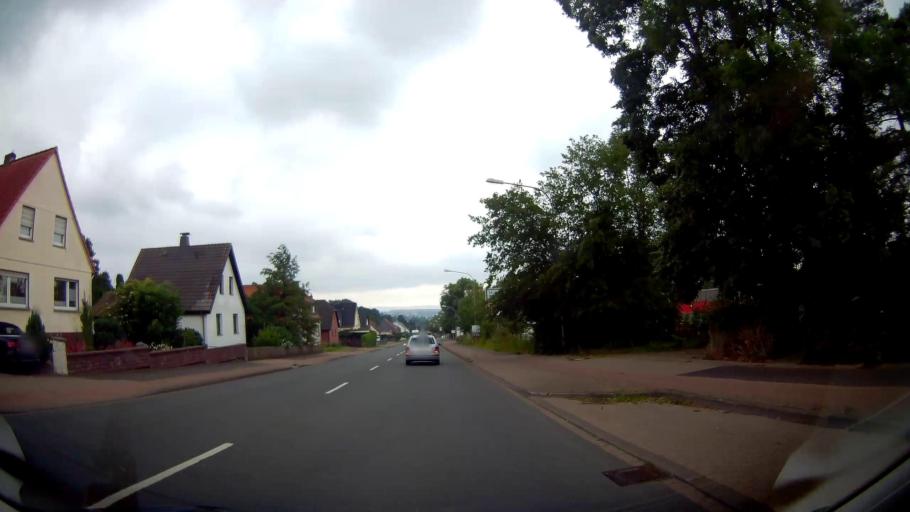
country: DE
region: North Rhine-Westphalia
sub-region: Regierungsbezirk Detmold
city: Herford
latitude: 52.1370
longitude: 8.6942
